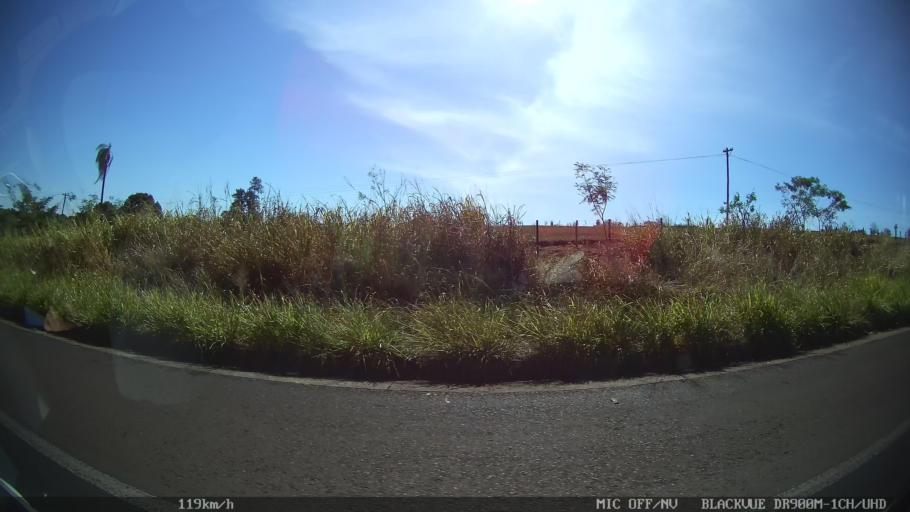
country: BR
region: Sao Paulo
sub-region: Barretos
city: Barretos
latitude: -20.6132
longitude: -48.7560
